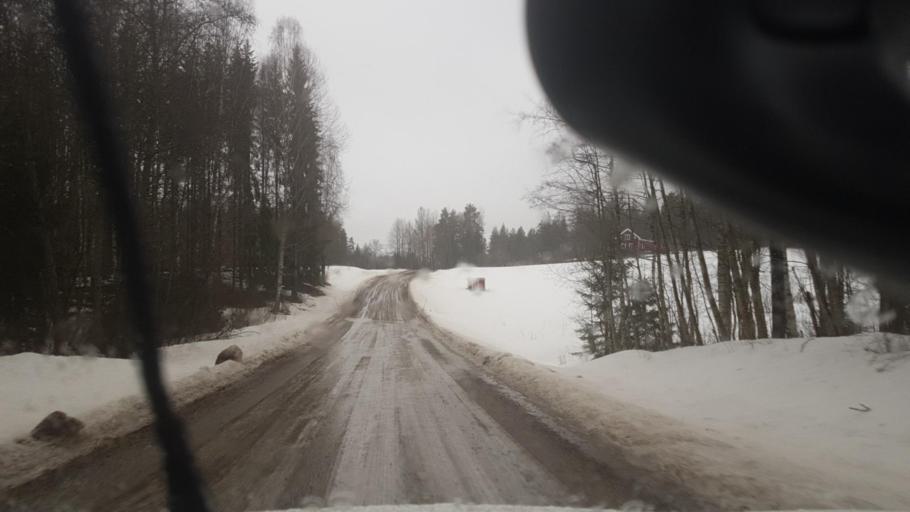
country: SE
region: Vaermland
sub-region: Eda Kommun
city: Amotfors
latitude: 59.8124
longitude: 12.3613
